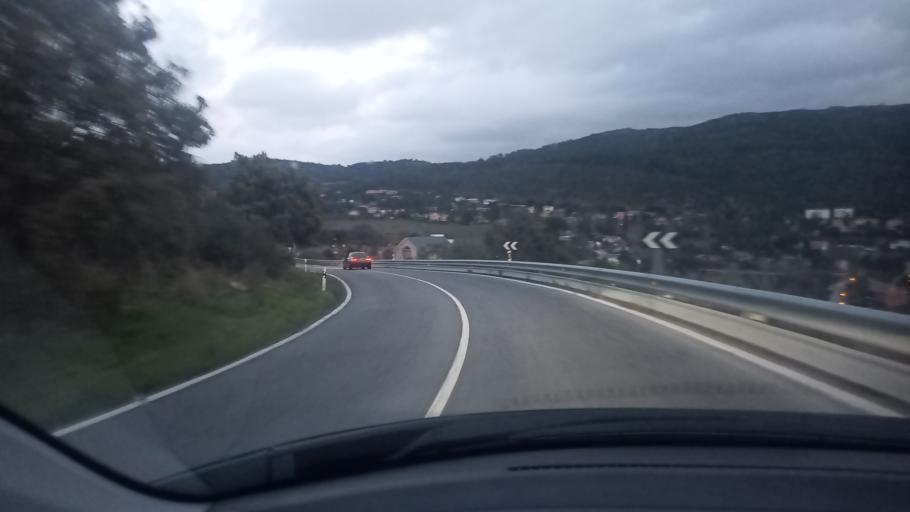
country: ES
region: Madrid
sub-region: Provincia de Madrid
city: Robledo de Chavela
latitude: 40.5089
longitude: -4.2399
